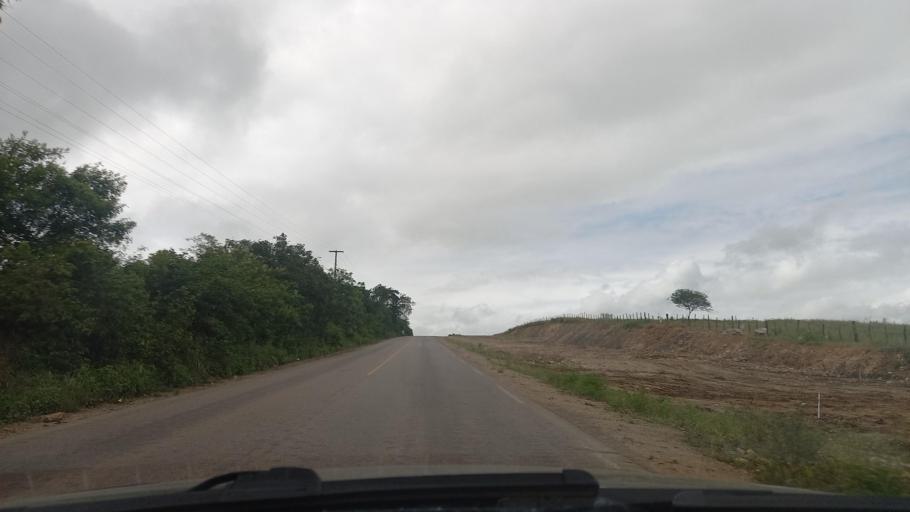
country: BR
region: Alagoas
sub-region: Batalha
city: Batalha
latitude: -9.6436
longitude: -37.1916
